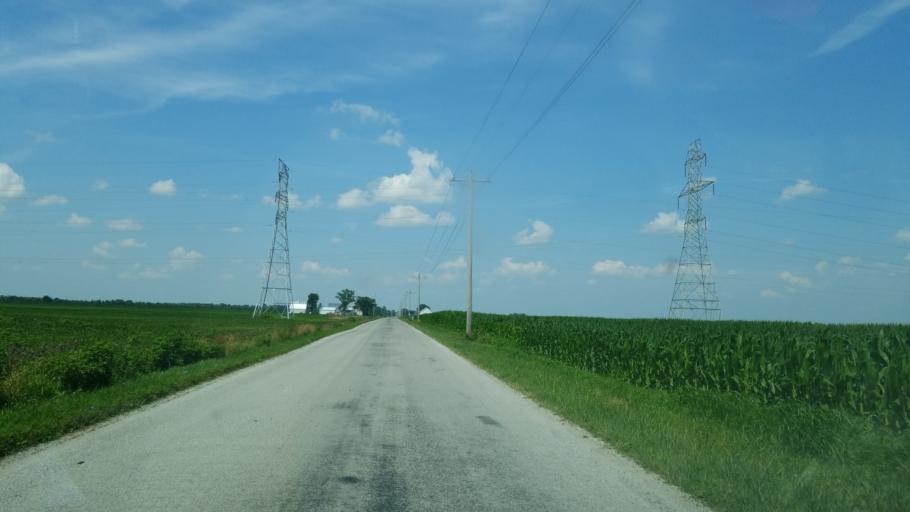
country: US
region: Ohio
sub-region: Seneca County
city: Fostoria
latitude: 41.2393
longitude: -83.4443
